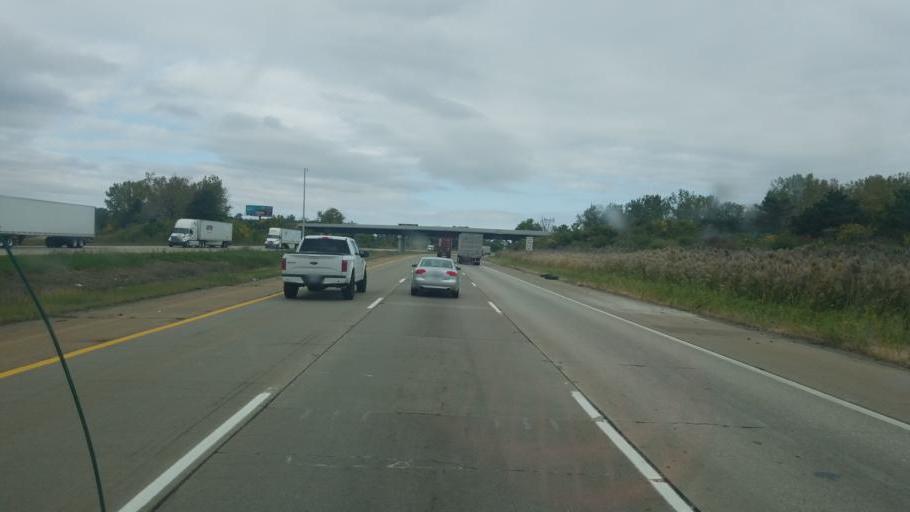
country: US
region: Michigan
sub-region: Monroe County
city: Luna Pier
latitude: 41.7664
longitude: -83.4807
